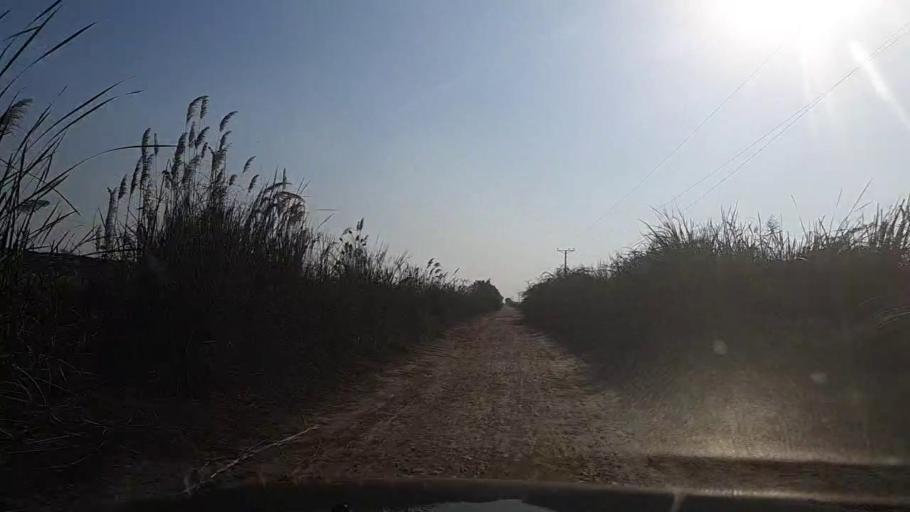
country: PK
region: Sindh
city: Gharo
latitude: 24.7252
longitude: 67.6934
